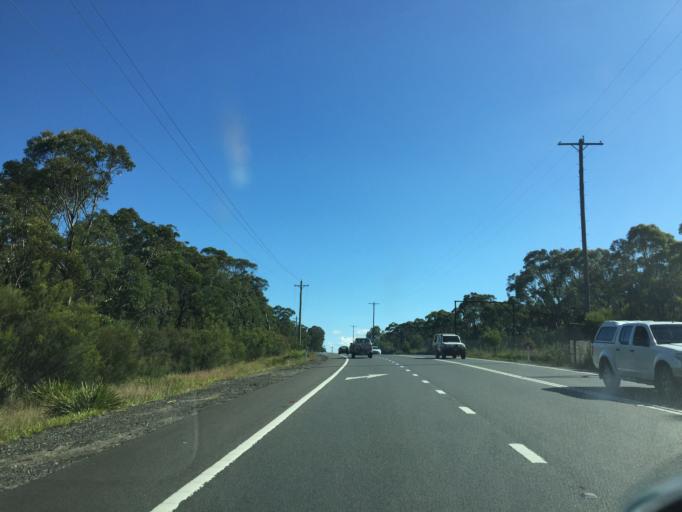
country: AU
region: New South Wales
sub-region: Blue Mountains Municipality
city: Blackheath
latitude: -33.6544
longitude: 150.2817
